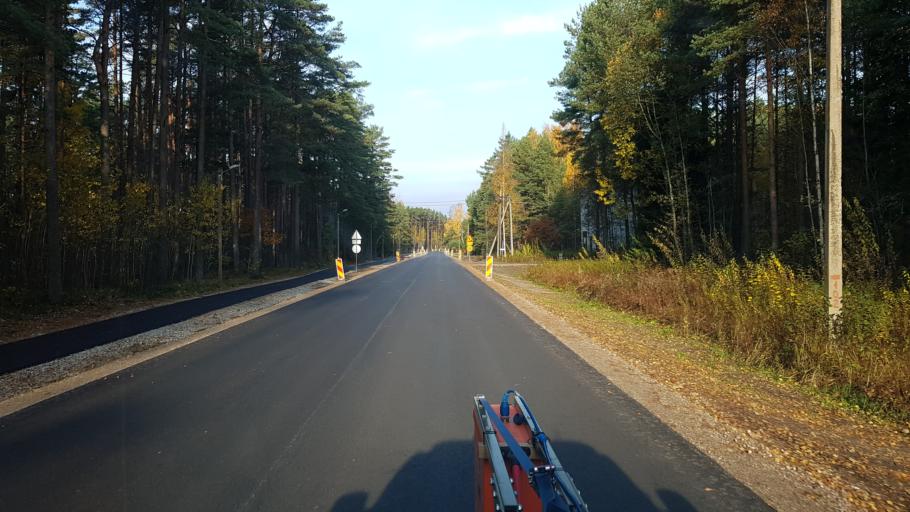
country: EE
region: Paernumaa
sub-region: Paikuse vald
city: Paikuse
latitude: 58.3593
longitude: 24.6110
